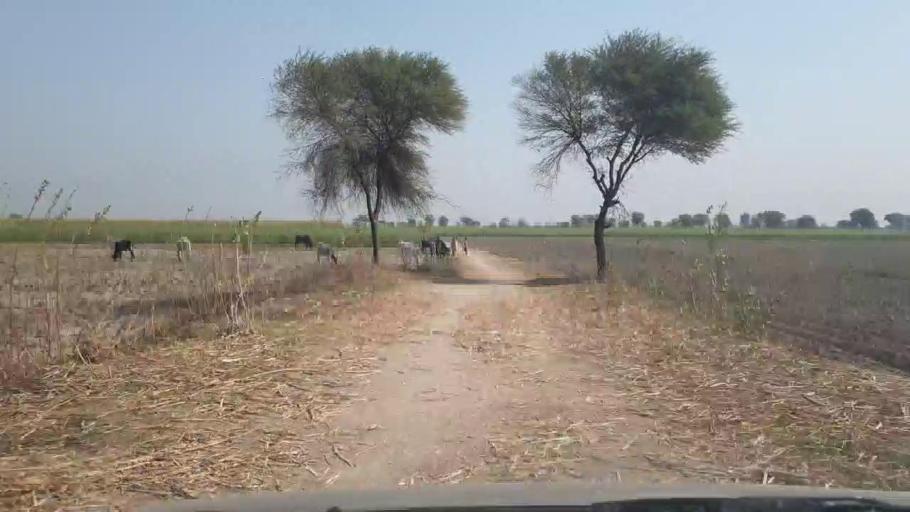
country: PK
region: Sindh
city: Mirwah Gorchani
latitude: 25.3044
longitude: 69.1580
